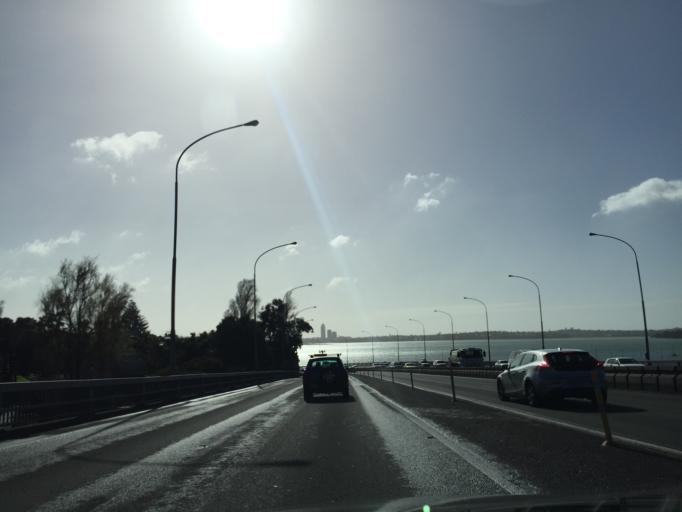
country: NZ
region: Auckland
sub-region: Auckland
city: North Shore
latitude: -36.8253
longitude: 174.7491
